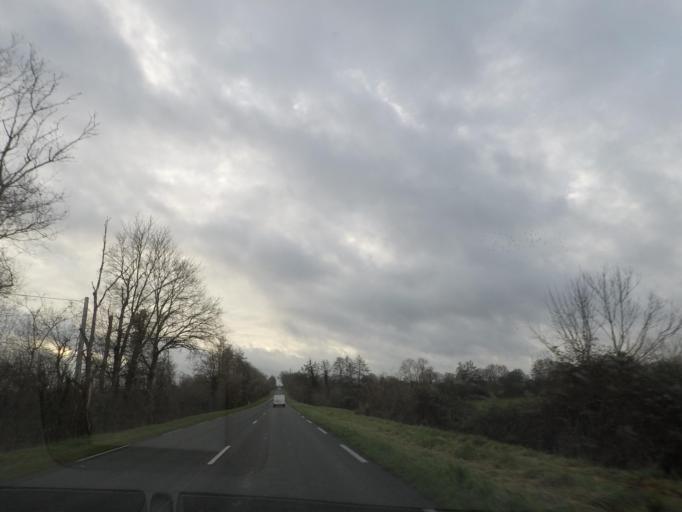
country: FR
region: Pays de la Loire
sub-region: Departement de la Sarthe
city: Vibraye
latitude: 48.0786
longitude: 0.7272
